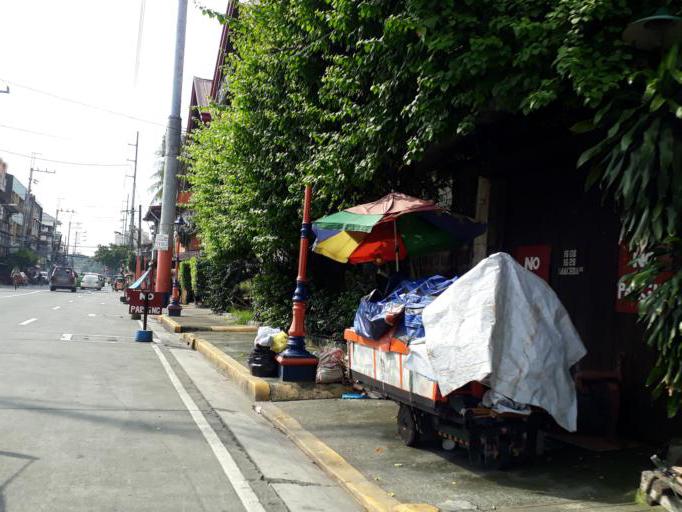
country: PH
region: Metro Manila
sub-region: City of Manila
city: Manila
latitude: 14.6218
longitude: 120.9907
